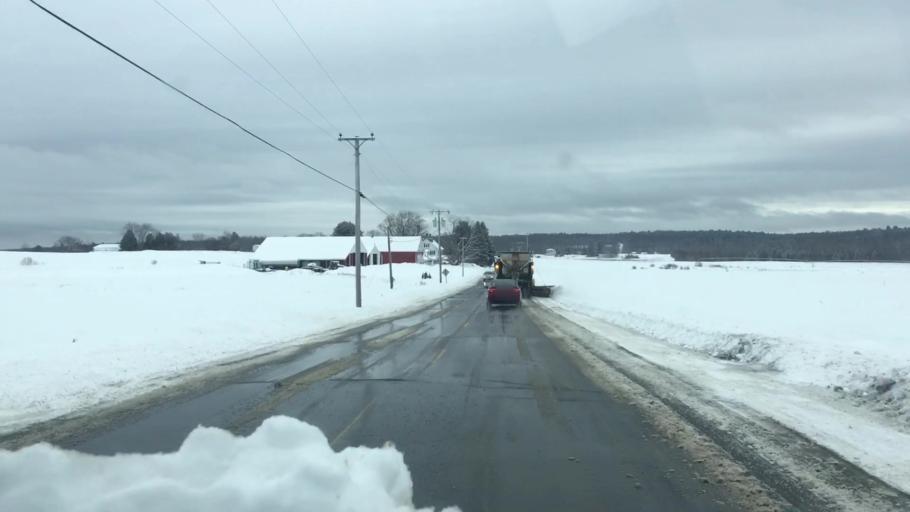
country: US
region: Maine
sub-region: Penobscot County
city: Garland
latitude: 44.9776
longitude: -69.0992
